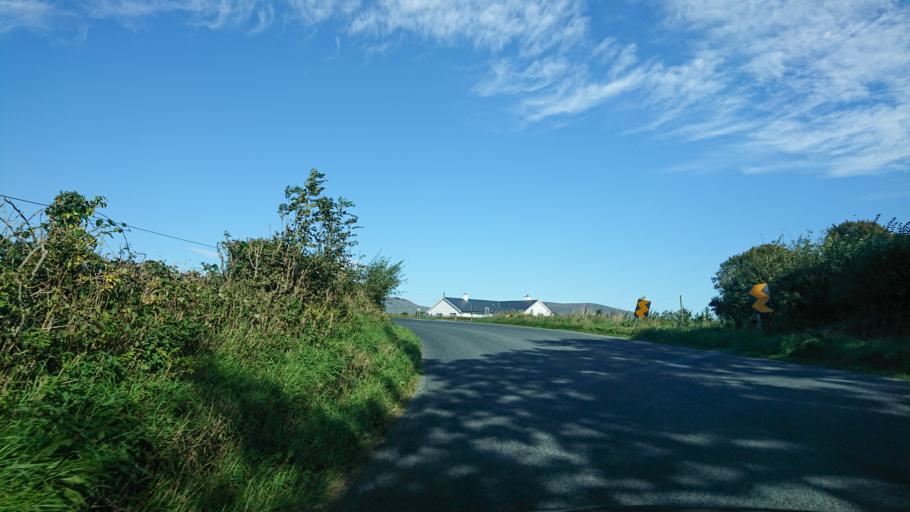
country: IE
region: Munster
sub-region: Waterford
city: Dungarvan
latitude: 52.1575
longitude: -7.6891
